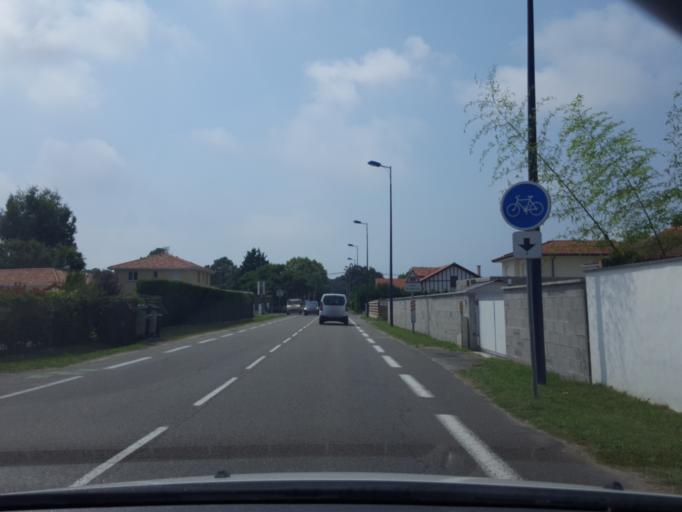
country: FR
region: Aquitaine
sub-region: Departement des Landes
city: Ondres
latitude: 43.5682
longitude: -1.4547
